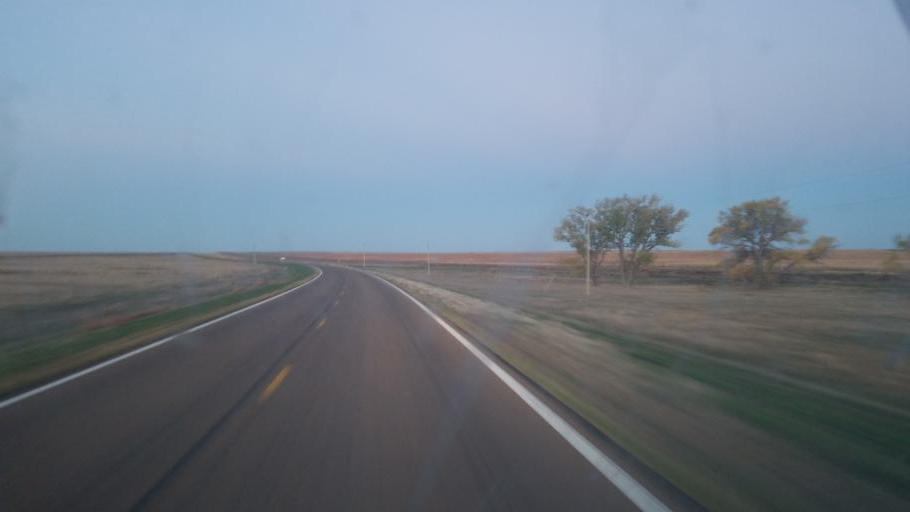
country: US
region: Kansas
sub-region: Wallace County
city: Sharon Springs
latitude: 39.0029
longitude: -101.3927
